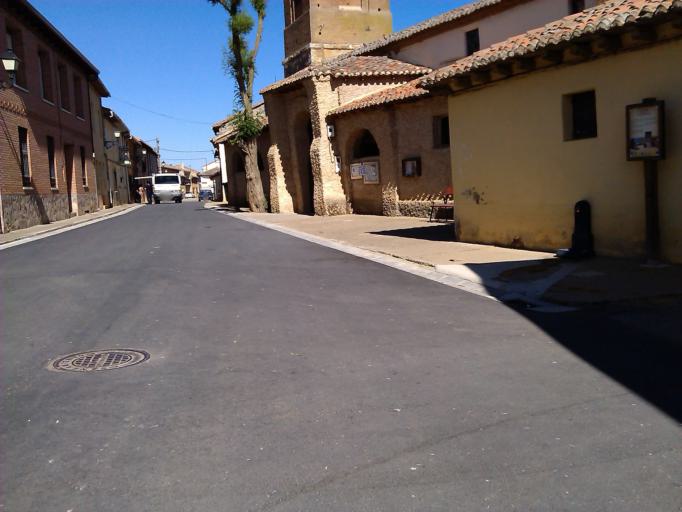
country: ES
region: Castille and Leon
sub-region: Provincia de Leon
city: Vallecillo
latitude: 42.4225
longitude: -5.2202
